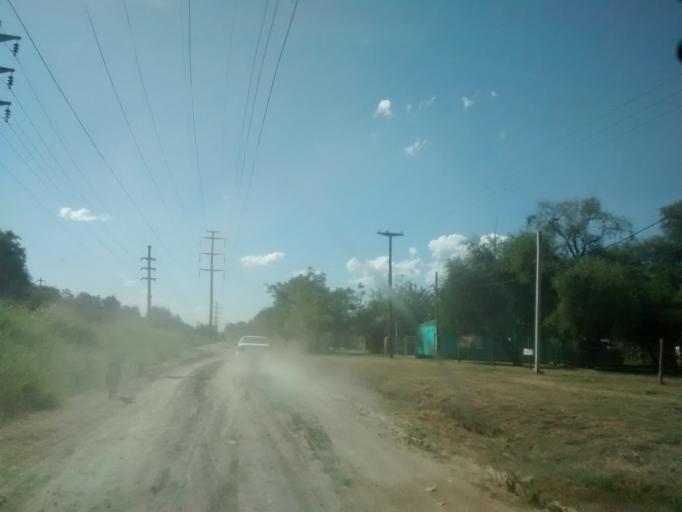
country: AR
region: Chaco
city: Fontana
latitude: -27.4054
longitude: -58.9951
